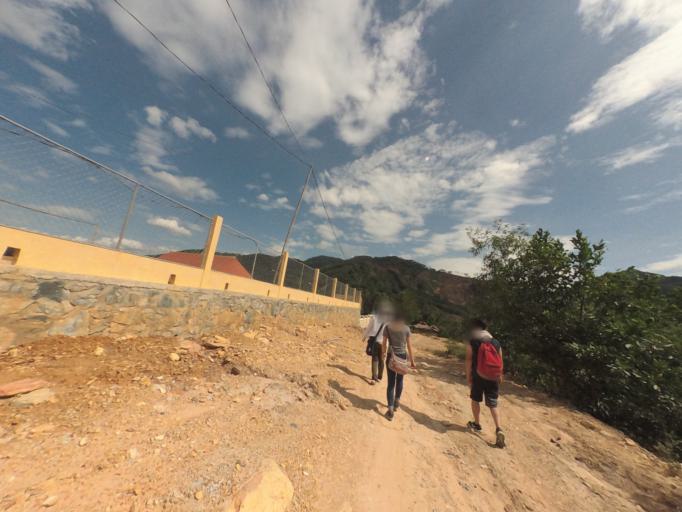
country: VN
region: Thua Thien-Hue
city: A Luoi
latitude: 16.3017
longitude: 107.3250
